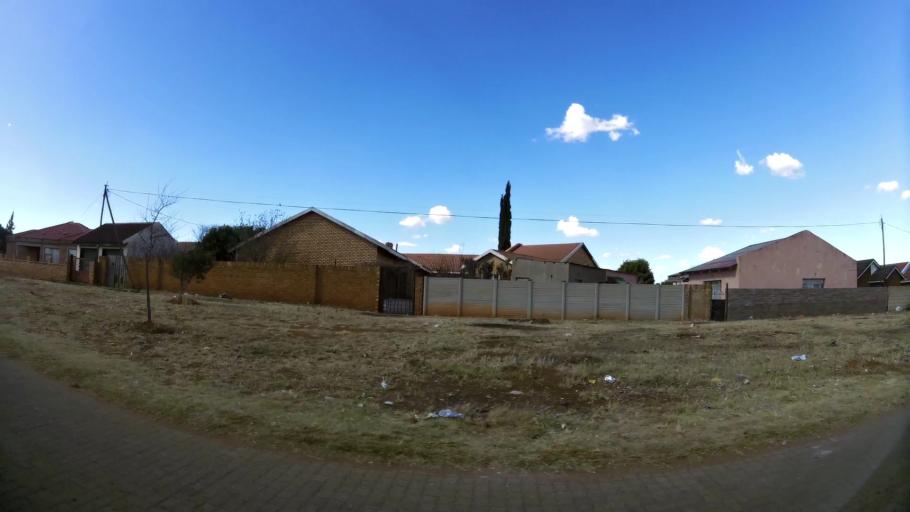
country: ZA
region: North-West
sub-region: Dr Kenneth Kaunda District Municipality
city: Klerksdorp
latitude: -26.8699
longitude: 26.5815
